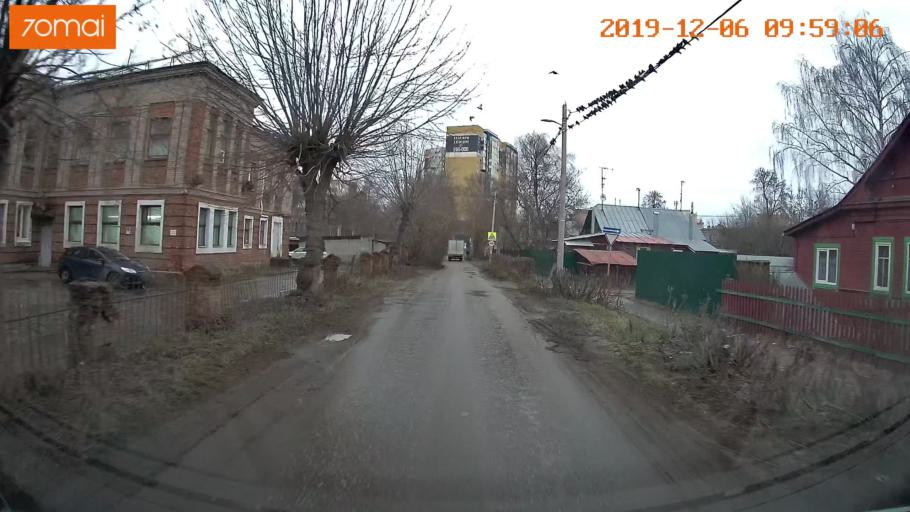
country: RU
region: Ivanovo
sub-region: Gorod Ivanovo
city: Ivanovo
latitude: 56.9846
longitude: 40.9769
